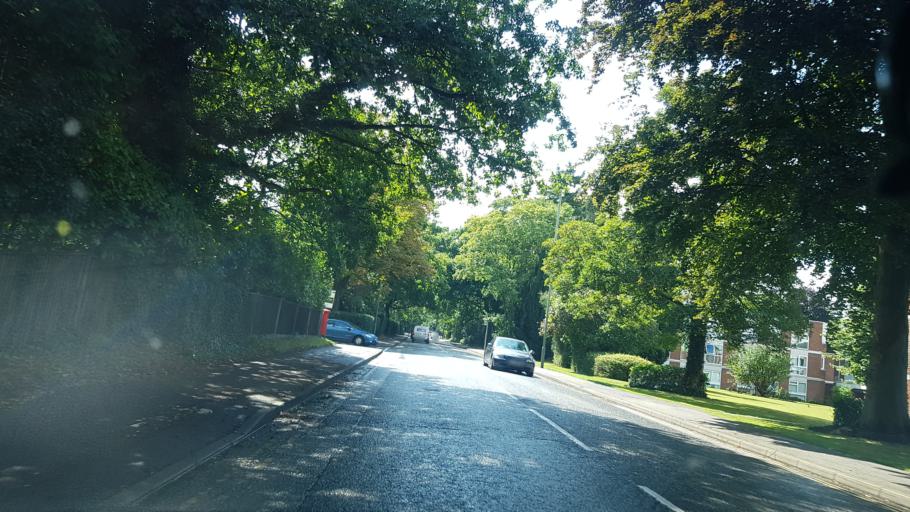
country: GB
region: England
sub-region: Surrey
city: West Byfleet
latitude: 51.3358
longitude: -0.5070
